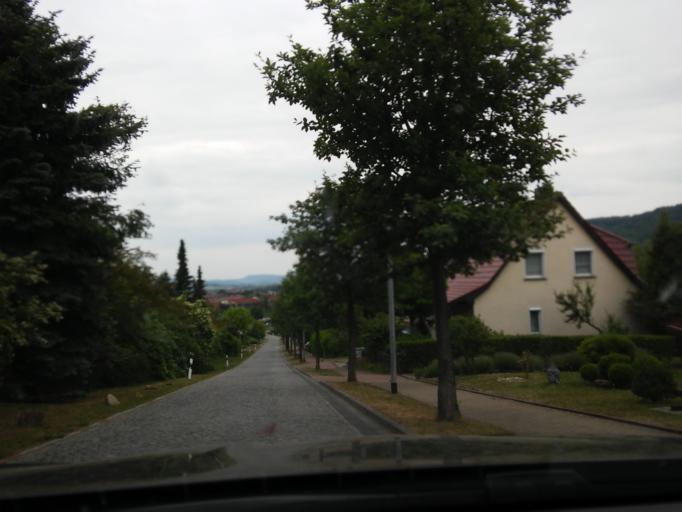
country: DE
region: Thuringia
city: Sondershausen
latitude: 51.3730
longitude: 10.8416
